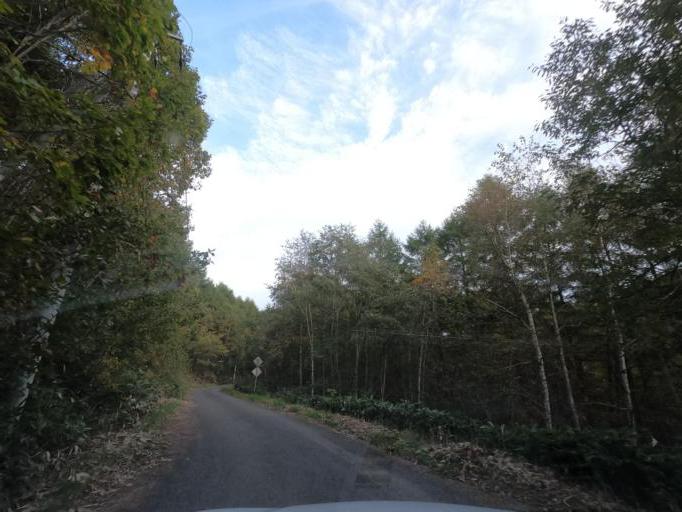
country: JP
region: Hokkaido
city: Obihiro
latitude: 42.5882
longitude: 143.3126
